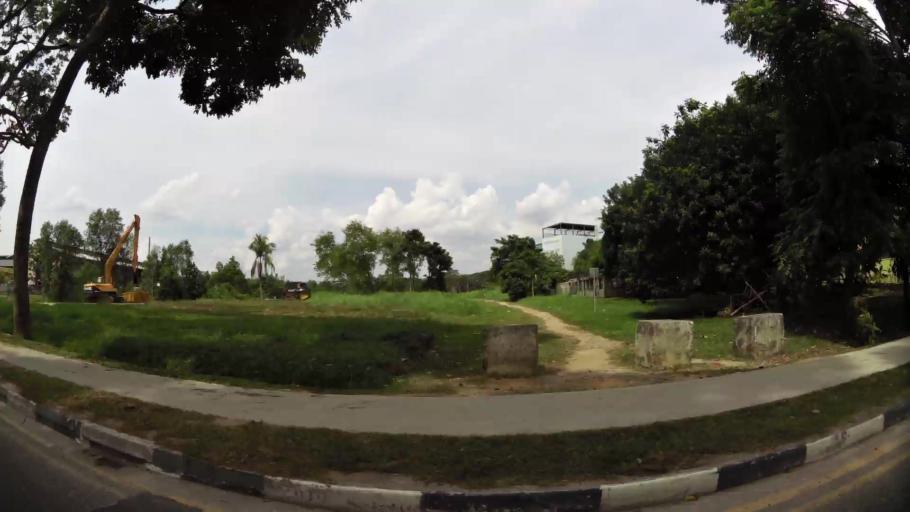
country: MY
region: Johor
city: Johor Bahru
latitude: 1.4077
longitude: 103.7550
